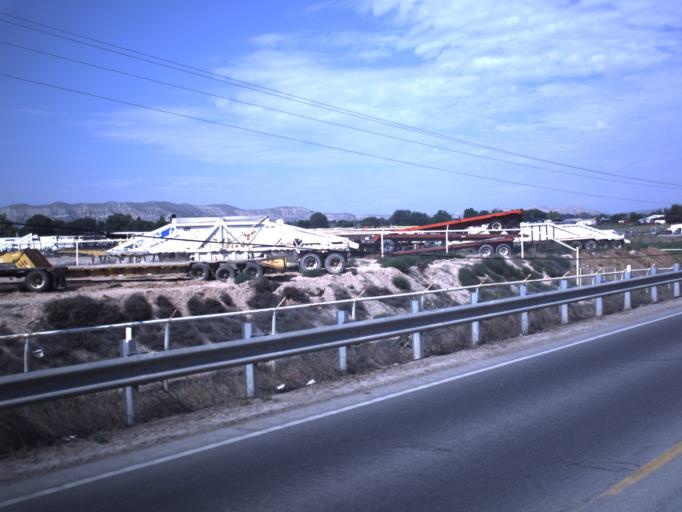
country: US
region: Utah
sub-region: Uintah County
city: Naples
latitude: 40.4010
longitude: -109.4682
